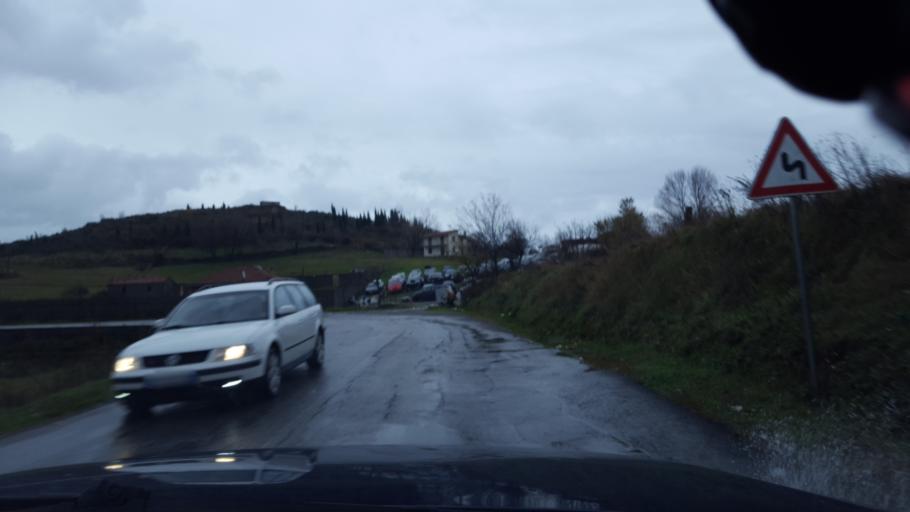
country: AL
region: Shkoder
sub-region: Rrethi i Shkodres
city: Berdica e Madhe
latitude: 42.0290
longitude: 19.4938
